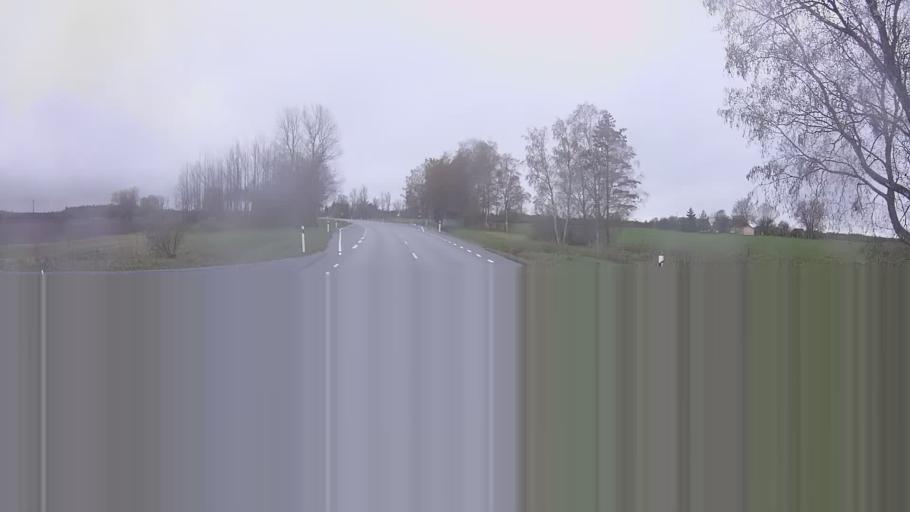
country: EE
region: Hiiumaa
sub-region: Kaerdla linn
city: Kardla
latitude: 58.9982
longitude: 22.5311
